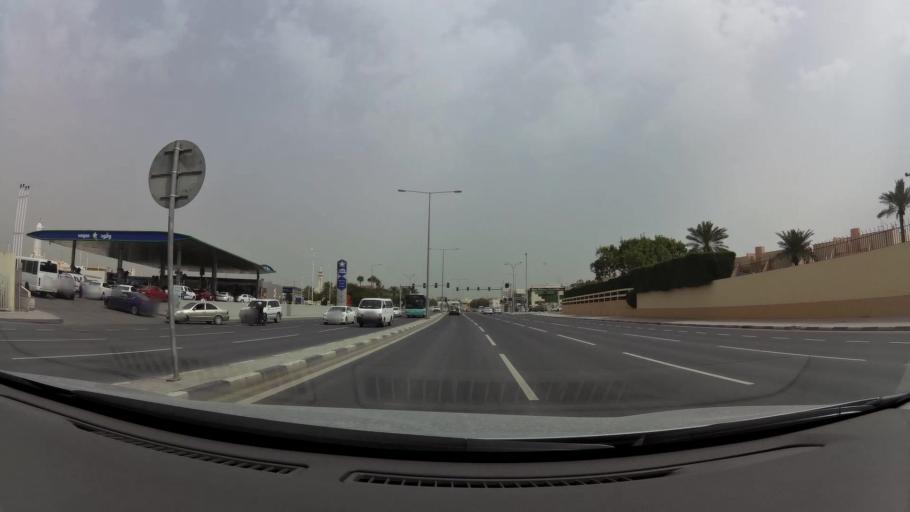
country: QA
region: Baladiyat ad Dawhah
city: Doha
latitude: 25.2580
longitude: 51.5370
